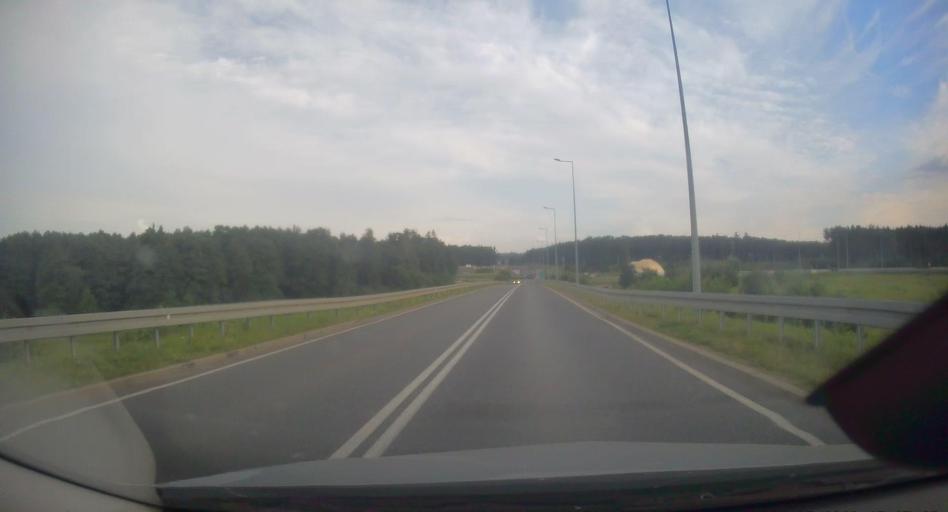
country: PL
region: Lesser Poland Voivodeship
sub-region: Powiat brzeski
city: Brzesko
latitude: 49.9919
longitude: 20.5913
